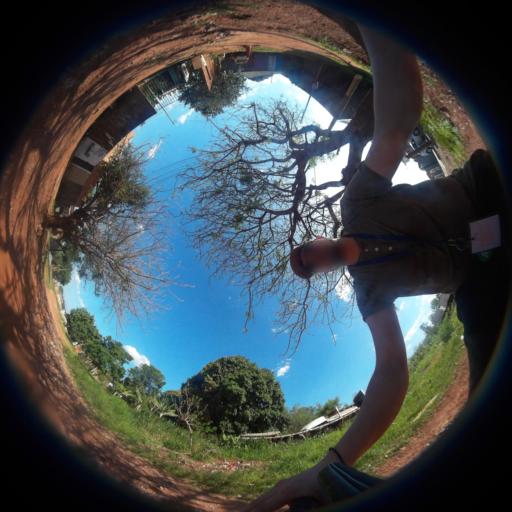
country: BR
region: Mato Grosso do Sul
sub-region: Ponta Pora
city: Ponta Pora
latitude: -22.5265
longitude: -55.7331
